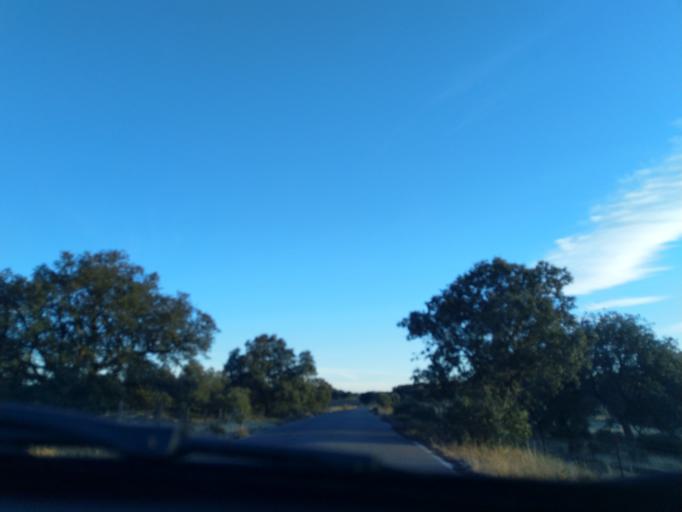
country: ES
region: Extremadura
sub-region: Provincia de Badajoz
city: Valverde de Llerena
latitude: 38.2392
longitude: -5.8241
